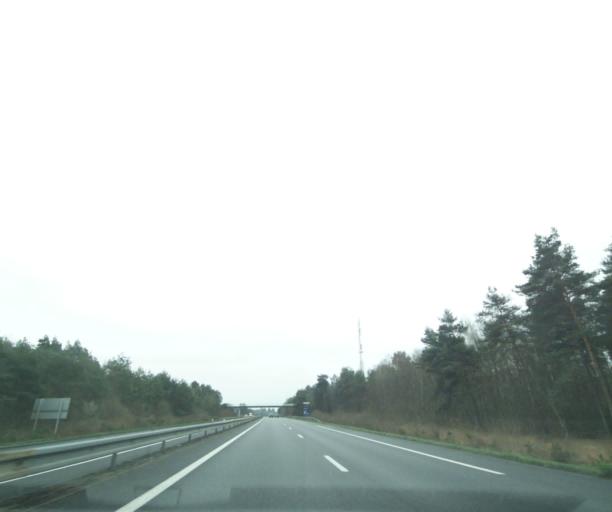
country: FR
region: Centre
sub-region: Departement du Loir-et-Cher
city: Chaumont-sur-Tharonne
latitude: 47.6432
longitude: 1.9445
